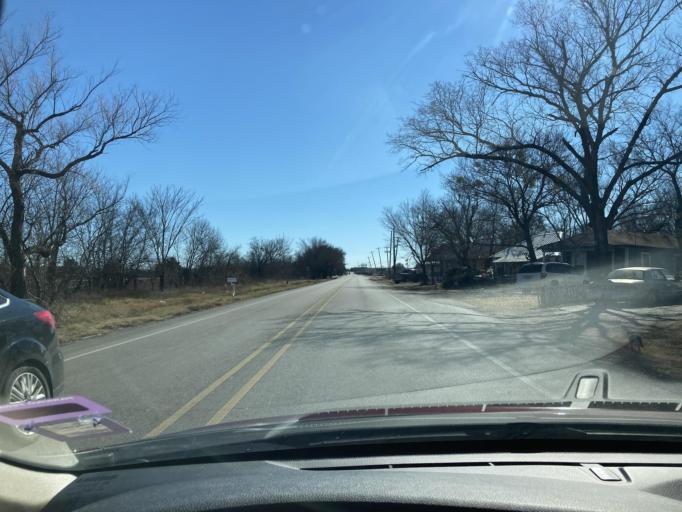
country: US
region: Texas
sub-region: Navarro County
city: Corsicana
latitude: 32.0798
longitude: -96.4630
